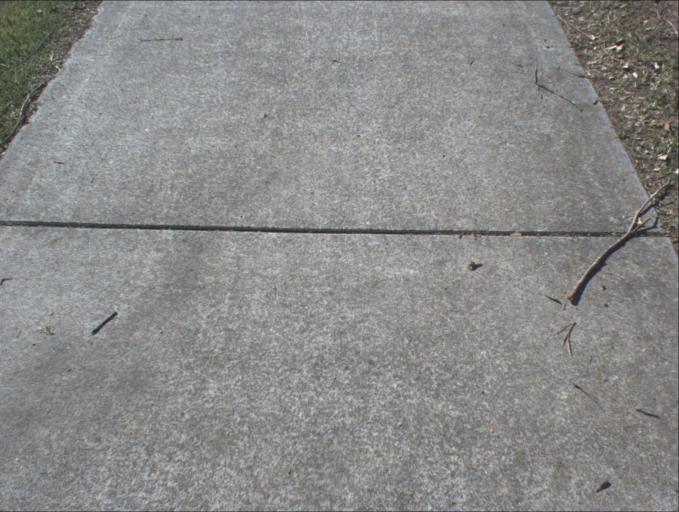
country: AU
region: Queensland
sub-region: Logan
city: Slacks Creek
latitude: -27.6339
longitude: 153.1586
